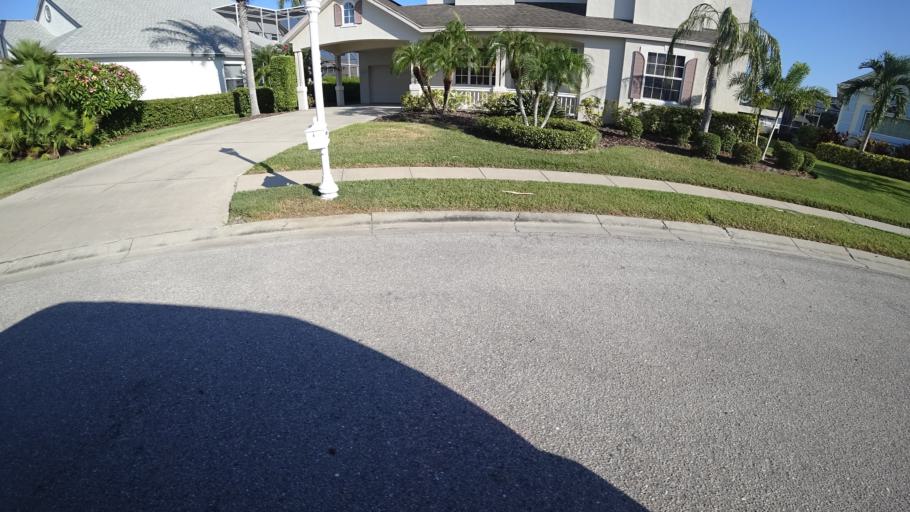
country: US
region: Florida
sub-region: Manatee County
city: Ellenton
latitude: 27.5058
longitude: -82.5076
